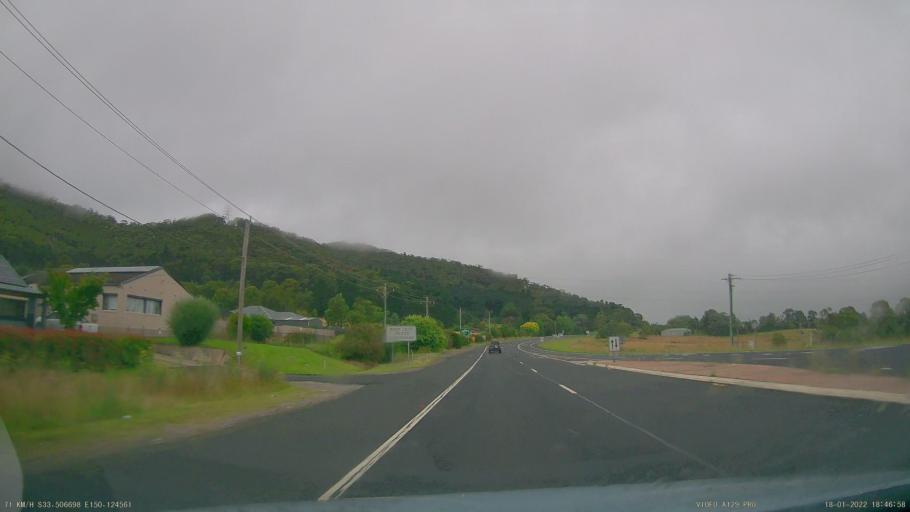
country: AU
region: New South Wales
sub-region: Lithgow
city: Bowenfels
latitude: -33.5070
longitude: 150.1245
